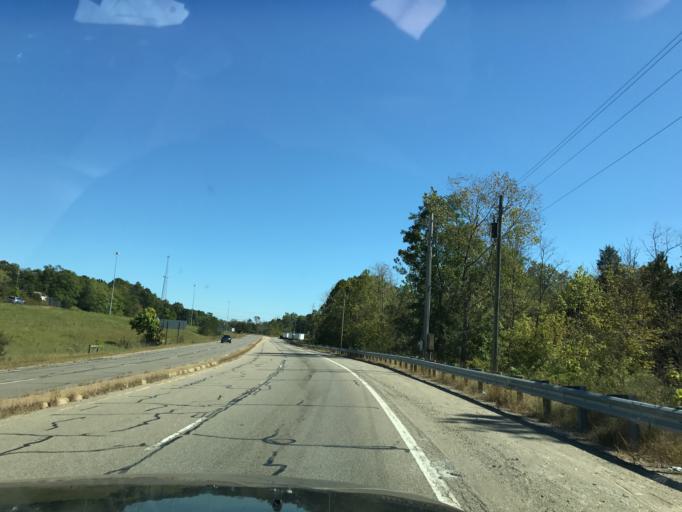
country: US
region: Ohio
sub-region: Muskingum County
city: Zanesville
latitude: 39.9470
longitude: -82.0448
